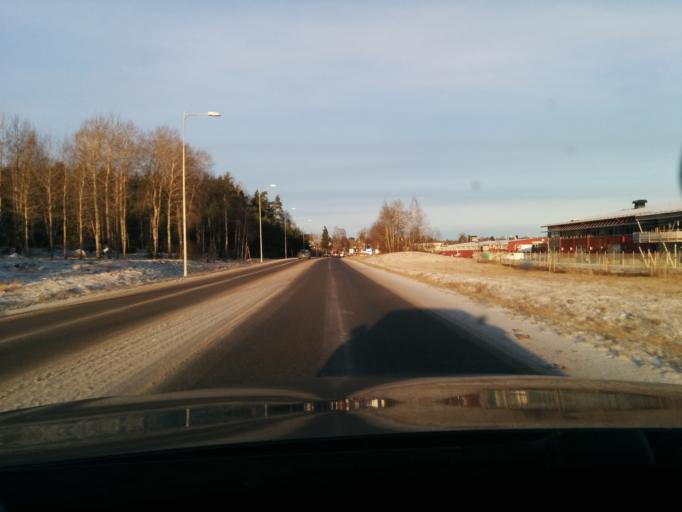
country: SE
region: Stockholm
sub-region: Taby Kommun
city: Taby
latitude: 59.4804
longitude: 18.0542
